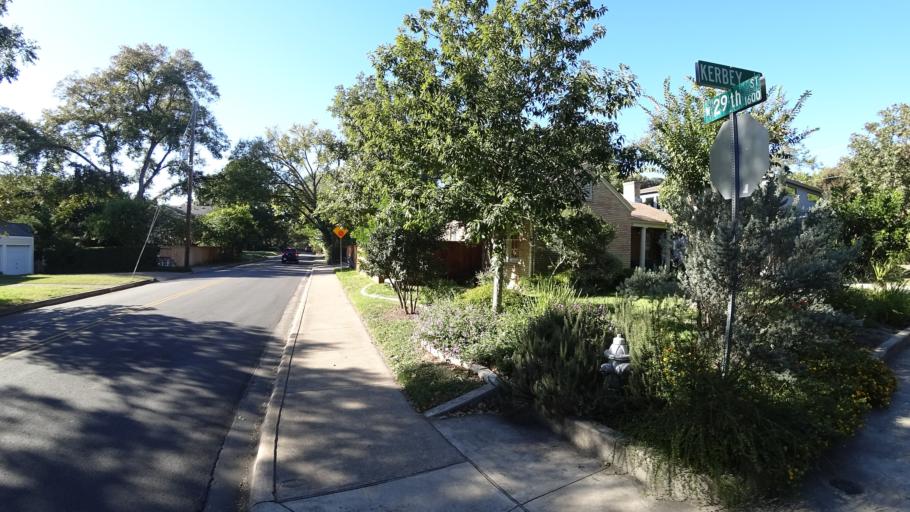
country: US
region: Texas
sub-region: Travis County
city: Austin
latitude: 30.3012
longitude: -97.7538
